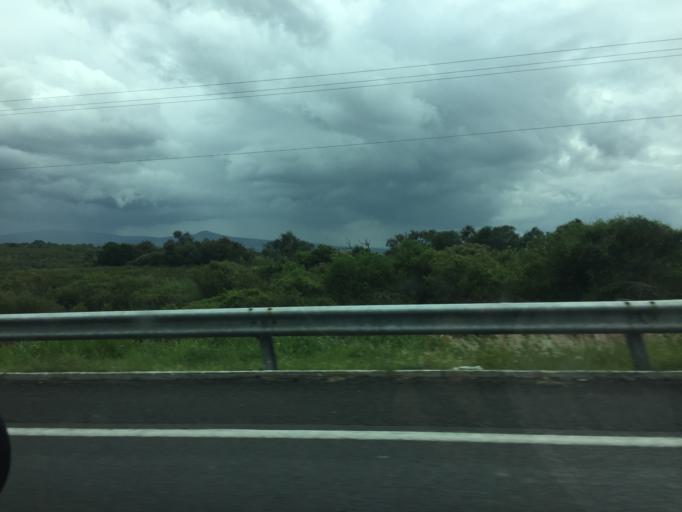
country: MX
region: Jalisco
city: Puente Grande
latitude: 20.6025
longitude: -103.1236
